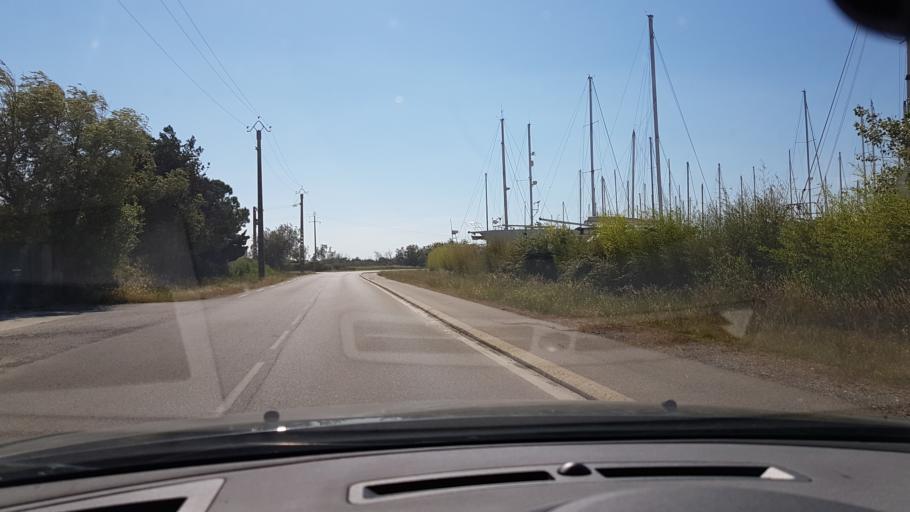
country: FR
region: Provence-Alpes-Cote d'Azur
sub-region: Departement des Bouches-du-Rhone
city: Port-Saint-Louis-du-Rhone
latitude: 43.3821
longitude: 4.8393
